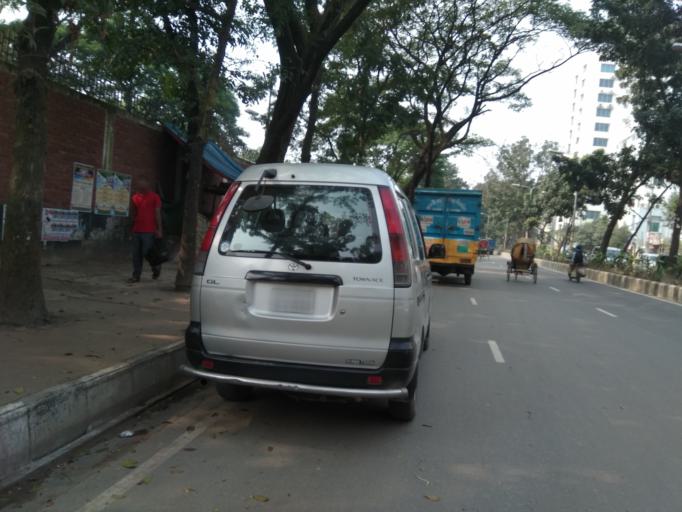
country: BD
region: Dhaka
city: Tungi
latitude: 23.8611
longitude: 90.3962
